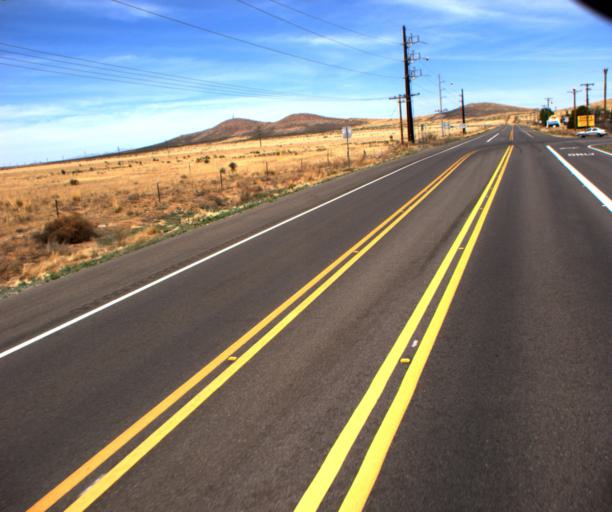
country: US
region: Arizona
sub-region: Cochise County
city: Willcox
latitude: 31.8829
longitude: -109.6951
